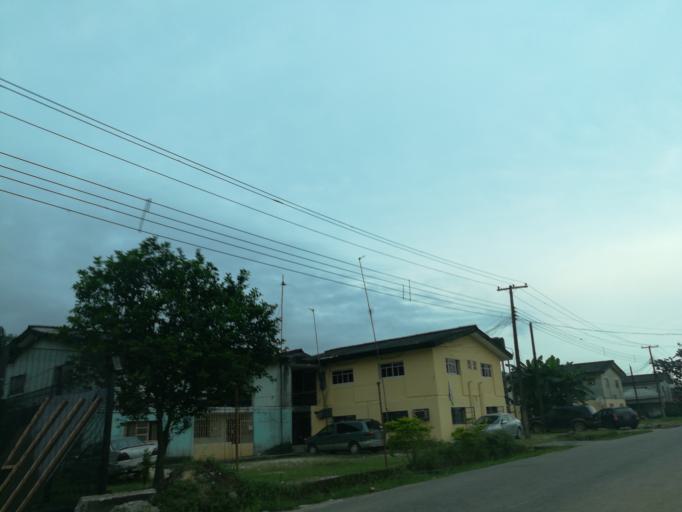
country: NG
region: Rivers
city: Port Harcourt
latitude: 4.8199
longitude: 7.0286
